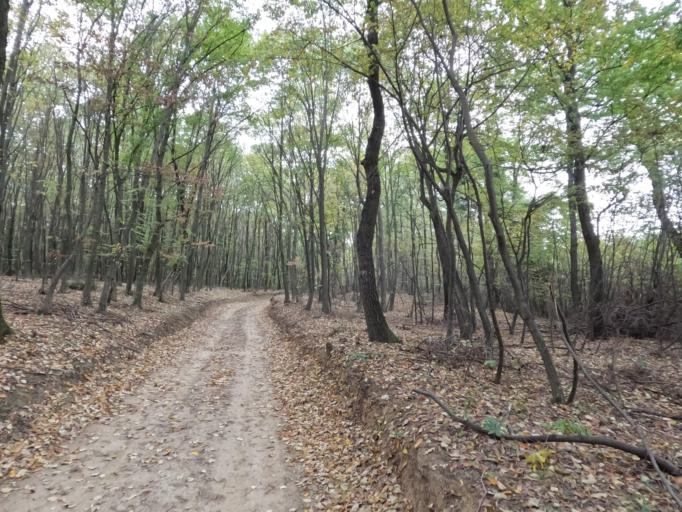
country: HU
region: Tolna
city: Szentgalpuszta
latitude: 46.3184
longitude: 18.6349
